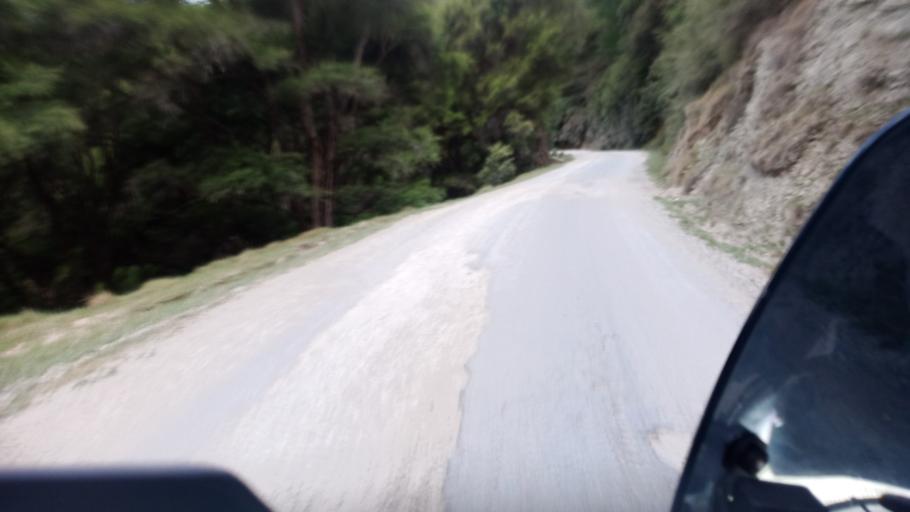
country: NZ
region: Gisborne
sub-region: Gisborne District
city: Gisborne
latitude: -38.4794
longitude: 177.9713
